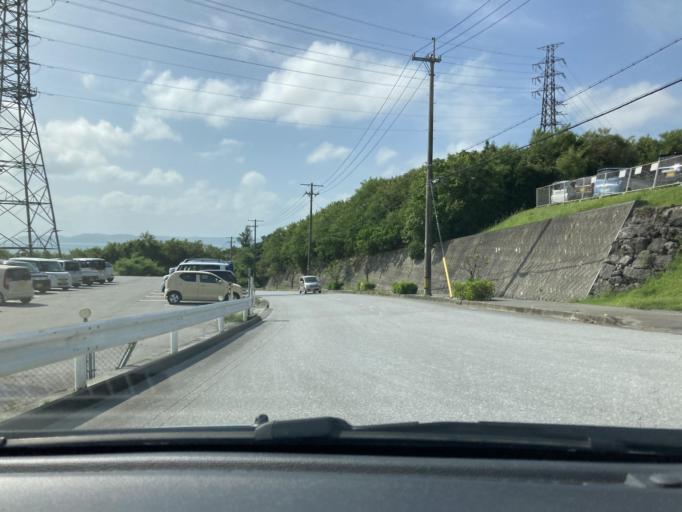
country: JP
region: Okinawa
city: Ginowan
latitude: 26.2765
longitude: 127.7969
